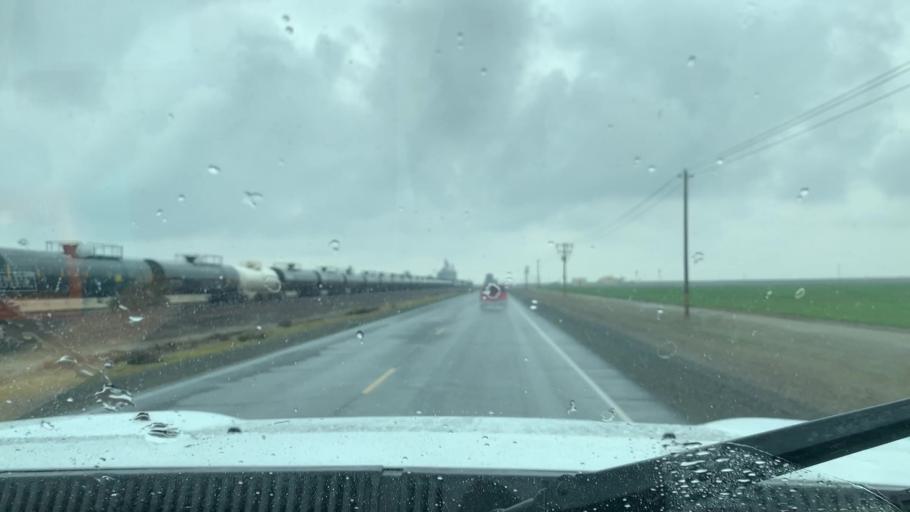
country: US
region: California
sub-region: Tulare County
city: Alpaugh
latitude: 35.9813
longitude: -119.4709
